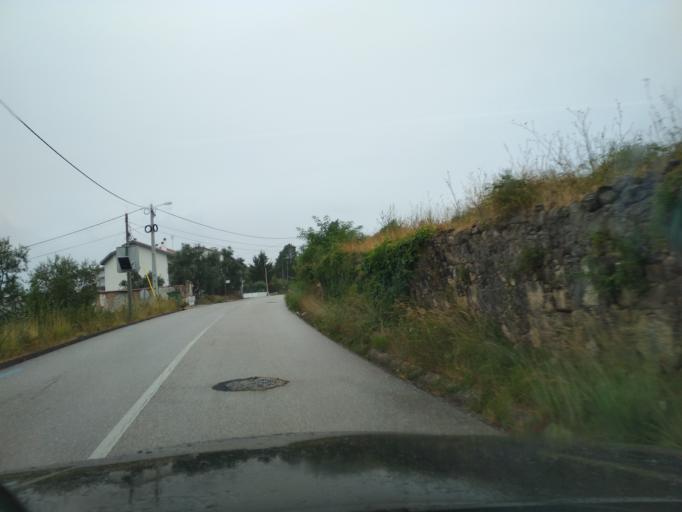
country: PT
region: Coimbra
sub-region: Coimbra
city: Coimbra
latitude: 40.1854
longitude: -8.4375
